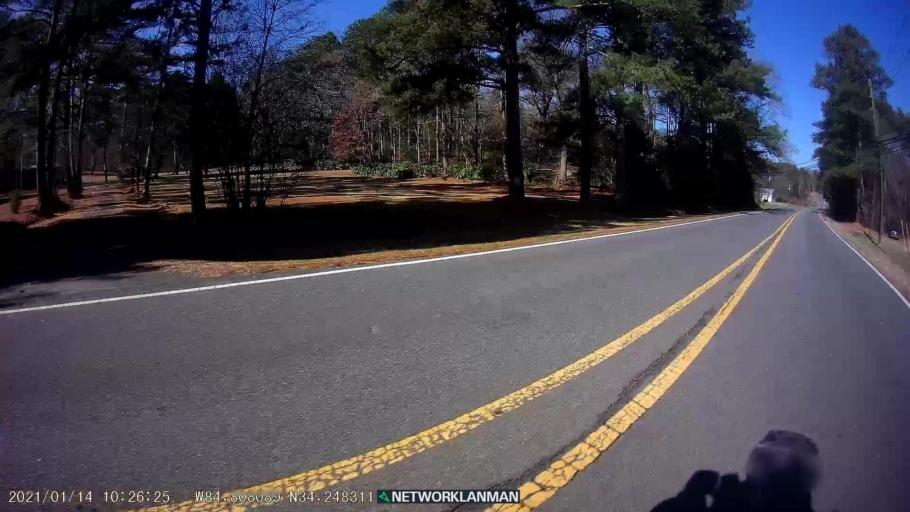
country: US
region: Georgia
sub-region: Bartow County
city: Cartersville
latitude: 34.2463
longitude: -84.8065
